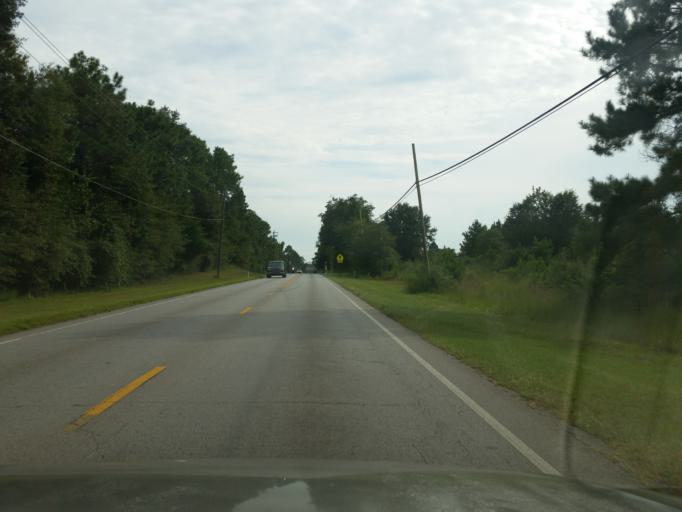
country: US
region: Florida
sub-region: Escambia County
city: Cantonment
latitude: 30.6276
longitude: -87.3216
